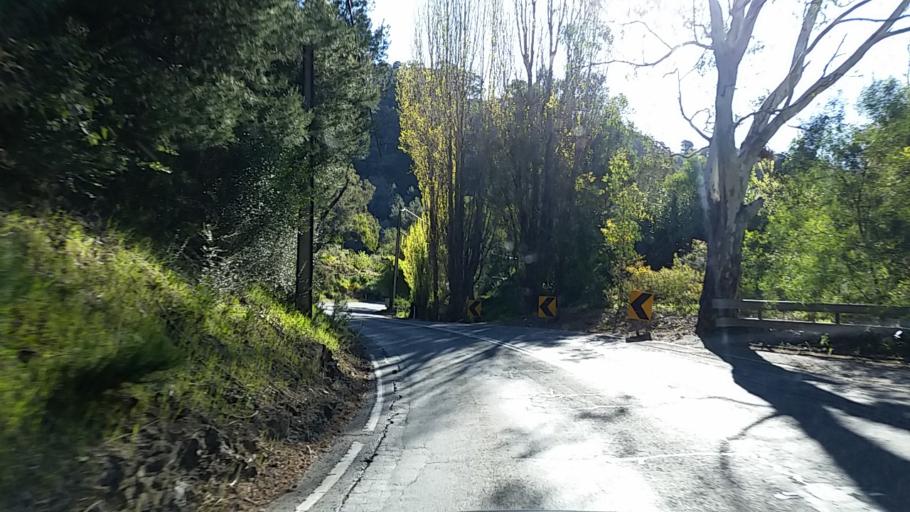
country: AU
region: South Australia
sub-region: Adelaide Hills
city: Adelaide Hills
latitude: -34.9216
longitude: 138.7000
